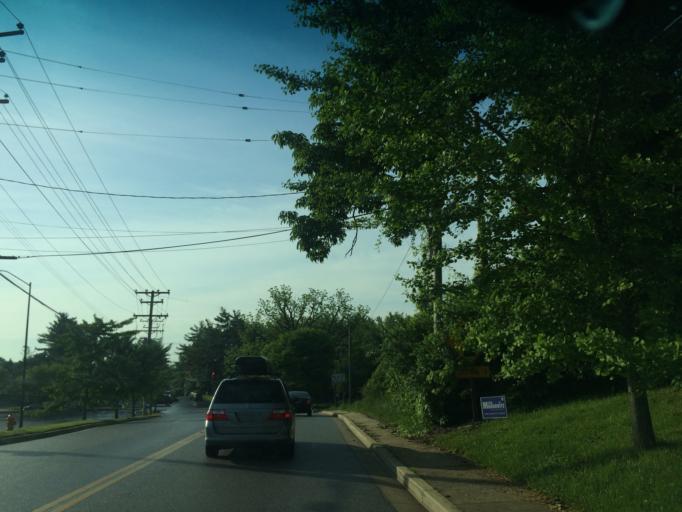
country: US
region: Maryland
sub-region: Howard County
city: Columbia
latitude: 39.2785
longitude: -76.8623
